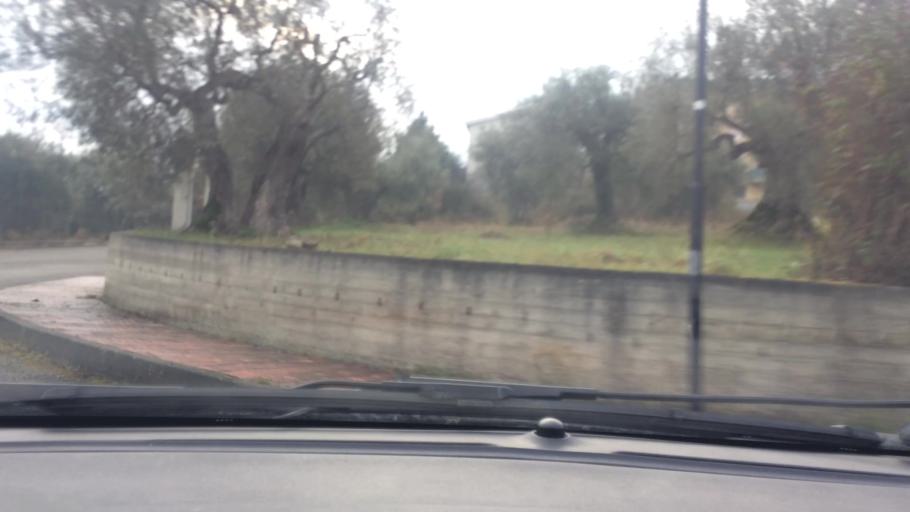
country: IT
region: Basilicate
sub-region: Provincia di Matera
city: San Mauro Forte
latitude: 40.4911
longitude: 16.2416
